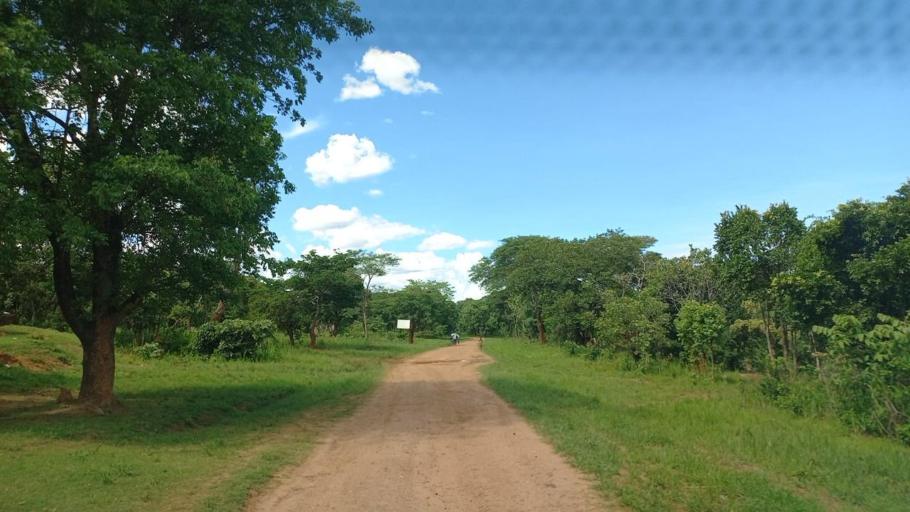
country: ZM
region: North-Western
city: Mwinilunga
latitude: -12.1834
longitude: 24.2819
